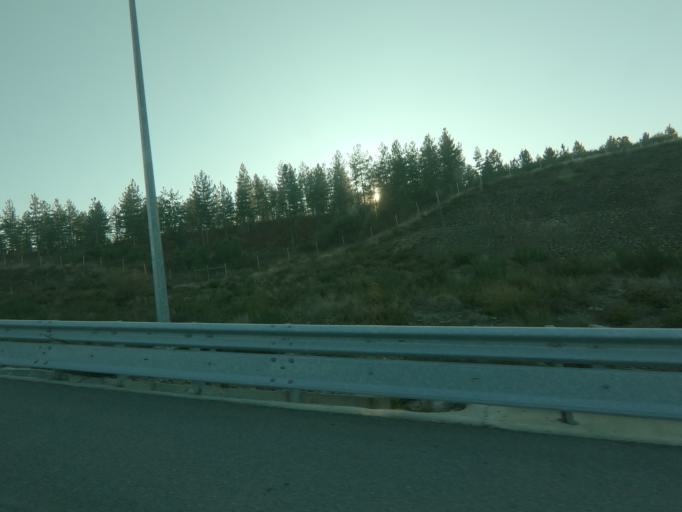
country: PT
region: Vila Real
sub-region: Santa Marta de Penaguiao
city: Santa Marta de Penaguiao
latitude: 41.2816
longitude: -7.8365
